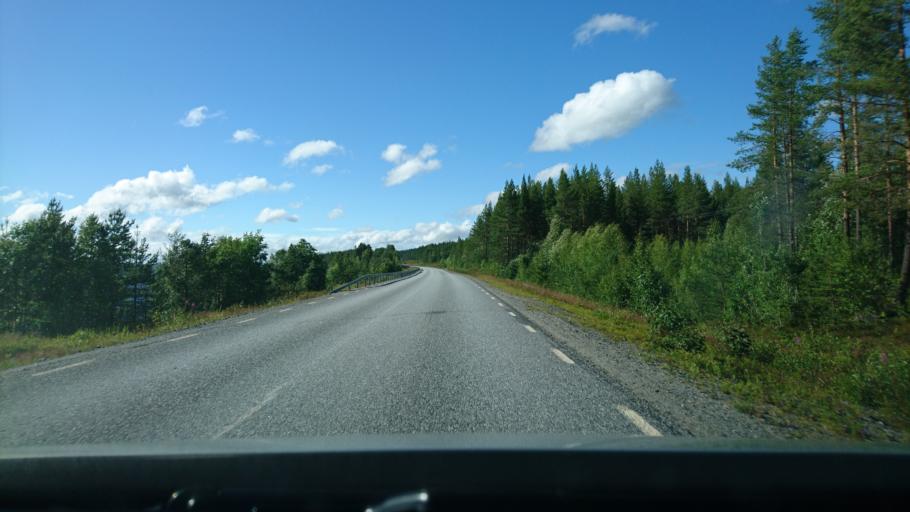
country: SE
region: Vaesterbotten
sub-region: Asele Kommun
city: Asele
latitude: 64.3467
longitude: 16.9996
